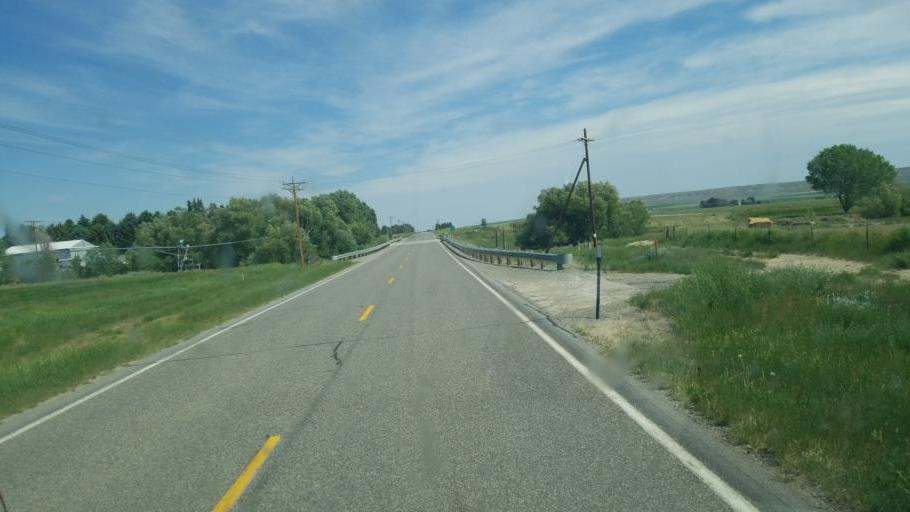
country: US
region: Wyoming
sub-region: Park County
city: Powell
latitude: 44.7426
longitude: -108.9327
